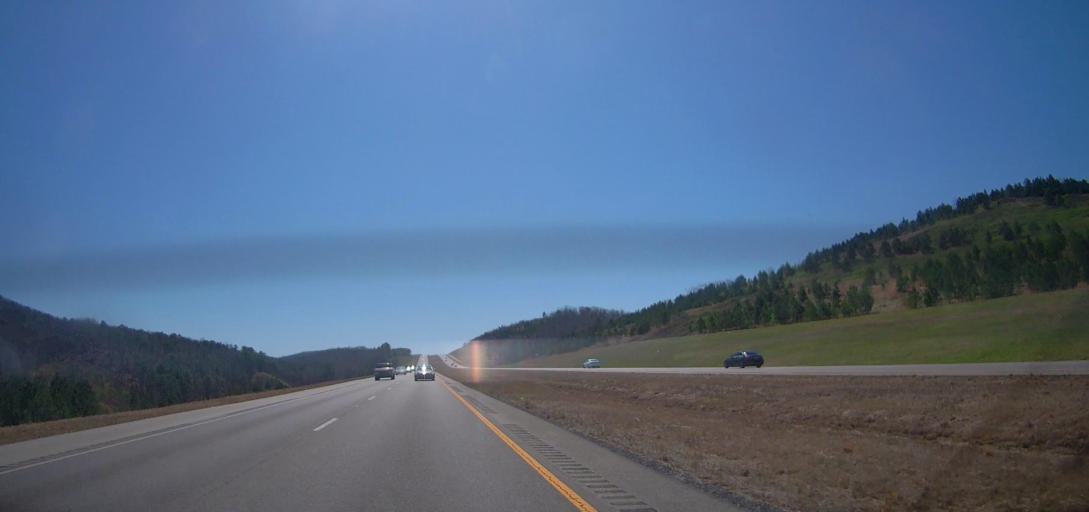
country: US
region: Alabama
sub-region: Calhoun County
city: Saks
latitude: 33.6972
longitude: -85.8074
